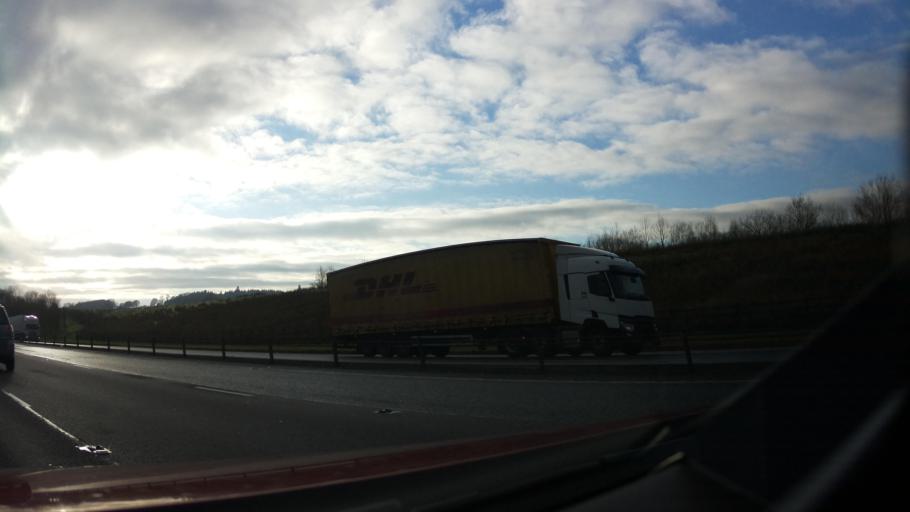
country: GB
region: Scotland
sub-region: Dumfries and Galloway
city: Moffat
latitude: 55.2664
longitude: -3.4172
